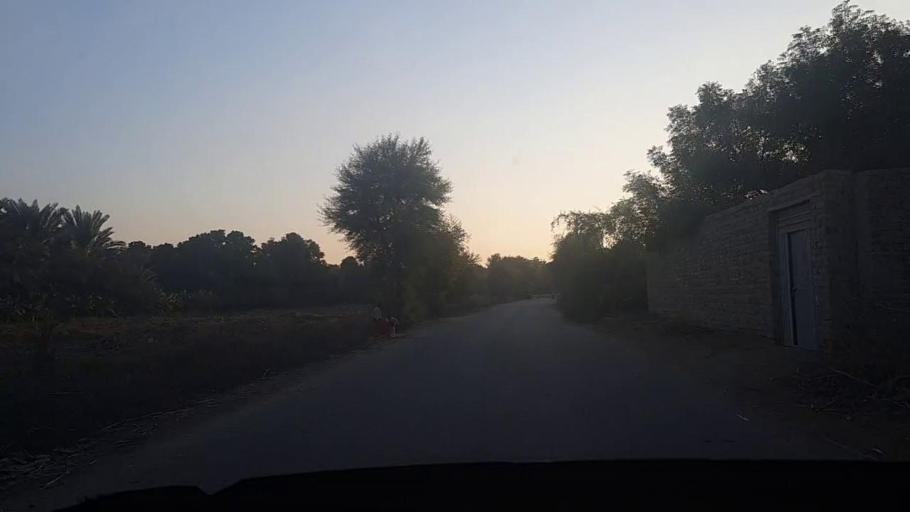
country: PK
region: Sindh
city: Sobhadero
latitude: 27.3384
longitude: 68.3786
